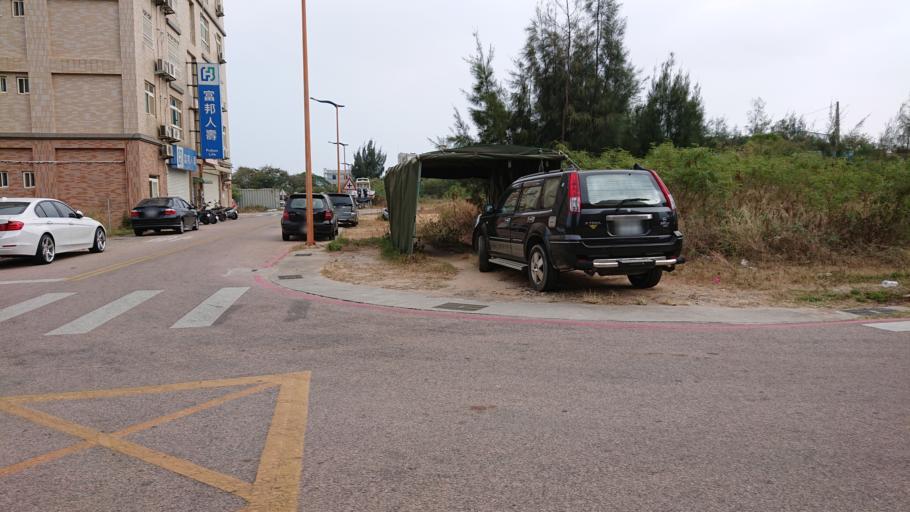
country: TW
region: Fukien
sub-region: Kinmen
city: Jincheng
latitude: 24.4399
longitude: 118.3197
